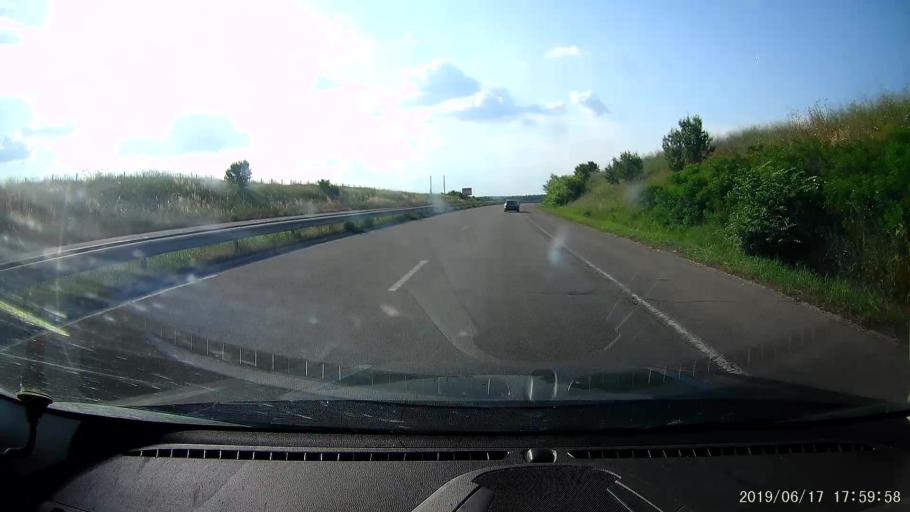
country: BG
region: Khaskovo
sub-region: Obshtina Svilengrad
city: Svilengrad
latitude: 41.7290
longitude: 26.2861
